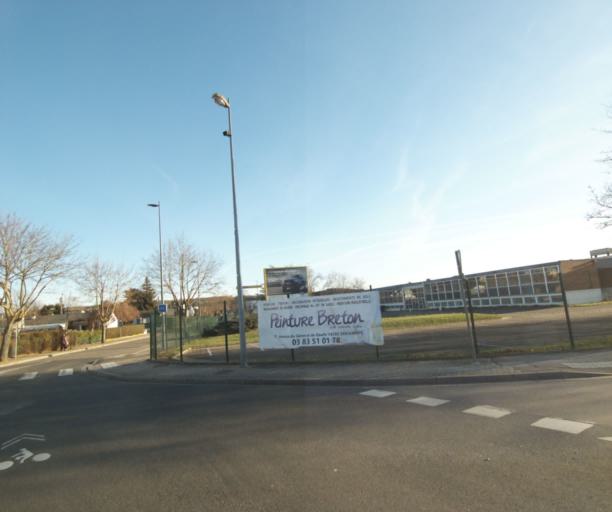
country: FR
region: Lorraine
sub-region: Departement de Meurthe-et-Moselle
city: Seichamps
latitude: 48.7117
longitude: 6.2528
